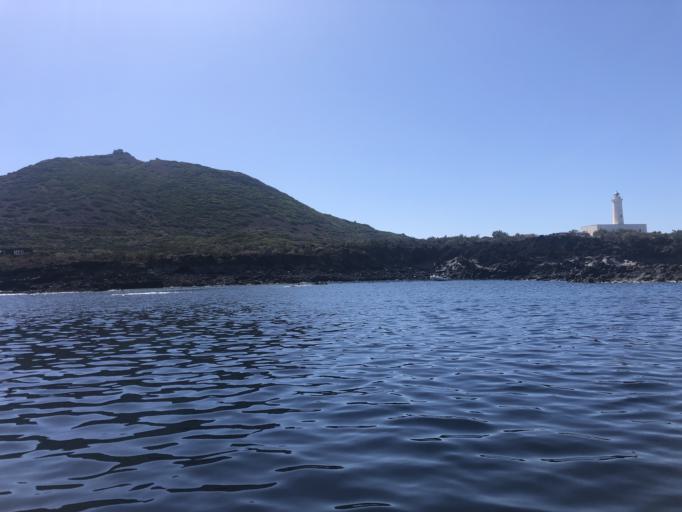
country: IT
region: Sicily
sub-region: Agrigento
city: Lampedusa
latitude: 35.8712
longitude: 12.8812
